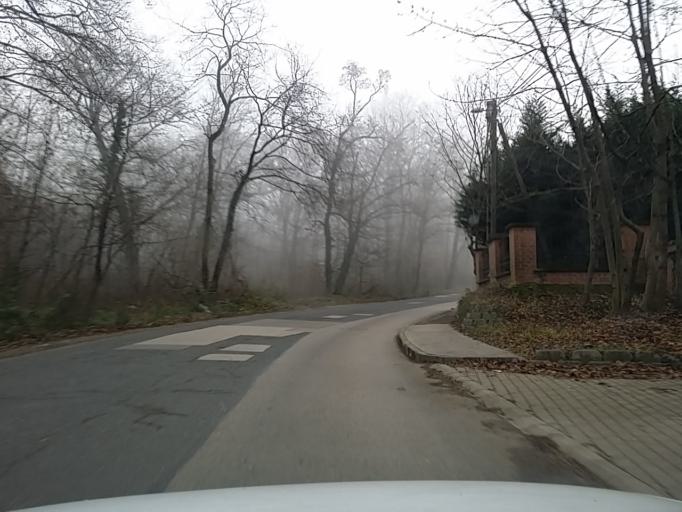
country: HU
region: Pest
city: Budakeszi
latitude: 47.5301
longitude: 18.9478
